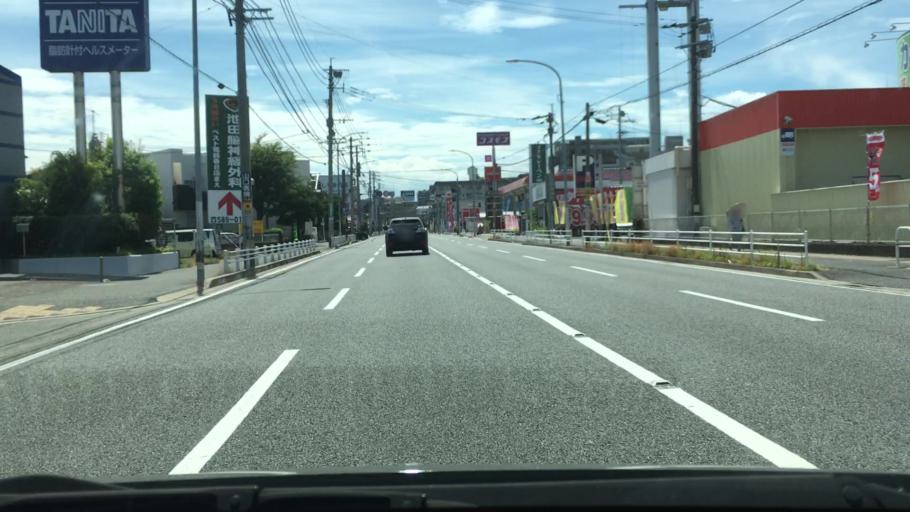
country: JP
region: Fukuoka
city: Onojo
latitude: 33.5524
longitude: 130.4566
